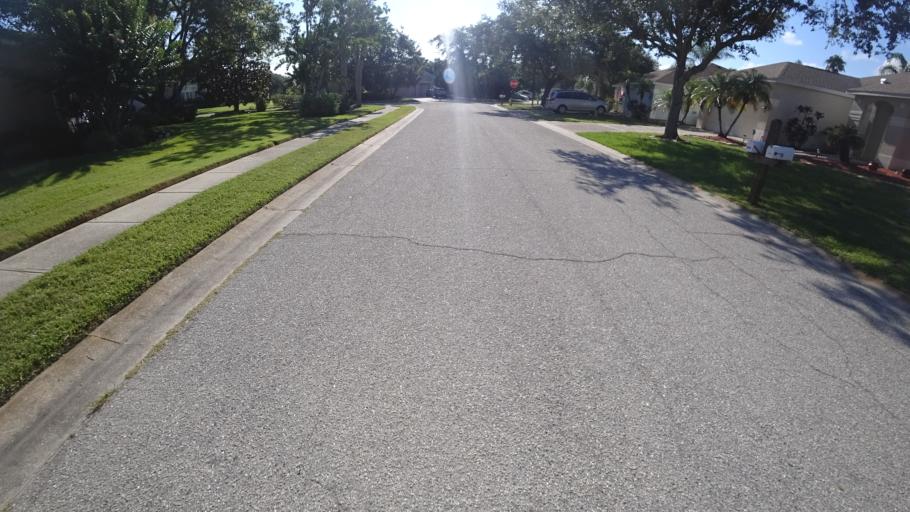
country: US
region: Florida
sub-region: Manatee County
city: Ellenton
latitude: 27.5004
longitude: -82.5132
